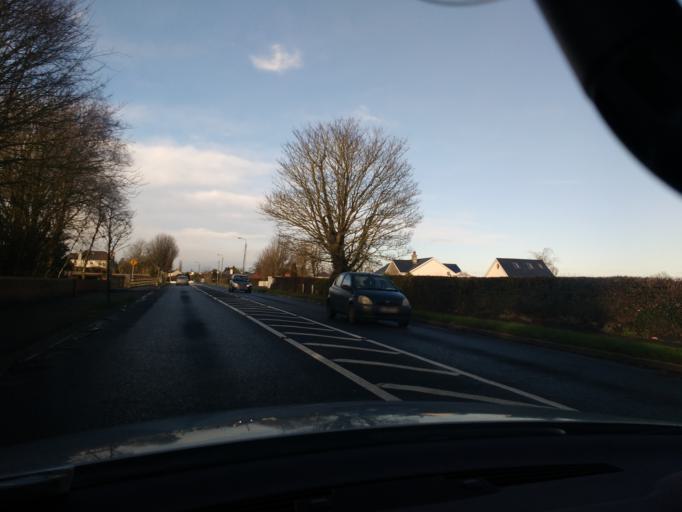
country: IE
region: Munster
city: Thurles
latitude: 52.6673
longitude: -7.8074
